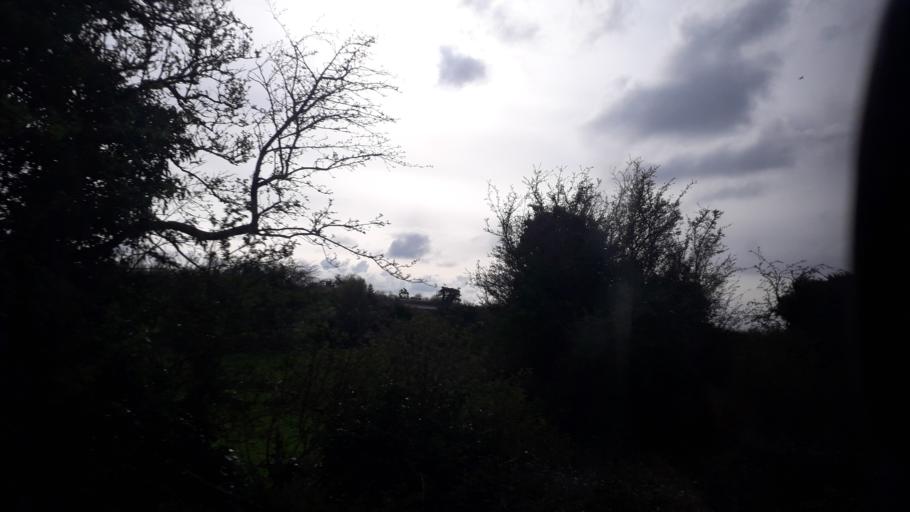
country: IE
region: Leinster
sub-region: Kildare
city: Kilcock
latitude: 53.4183
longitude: -6.7062
